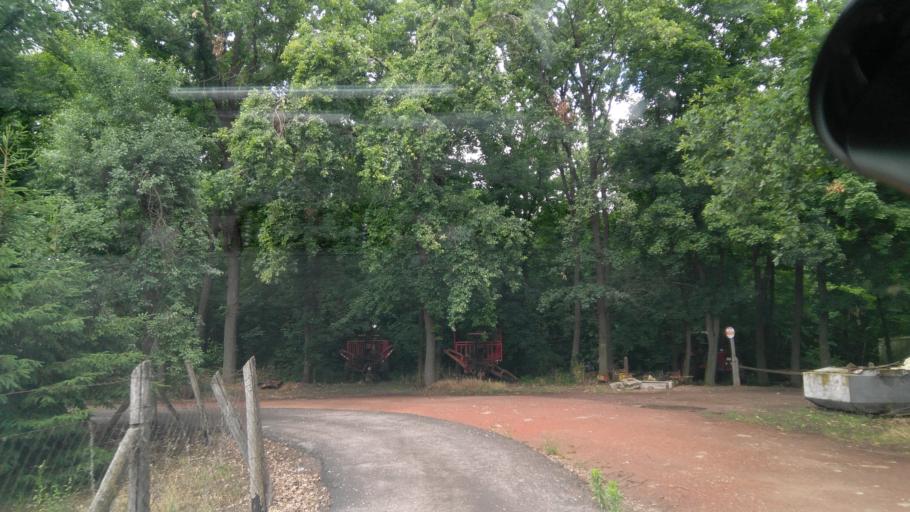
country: HU
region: Bekes
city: Bekescsaba
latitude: 46.6769
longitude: 21.1793
